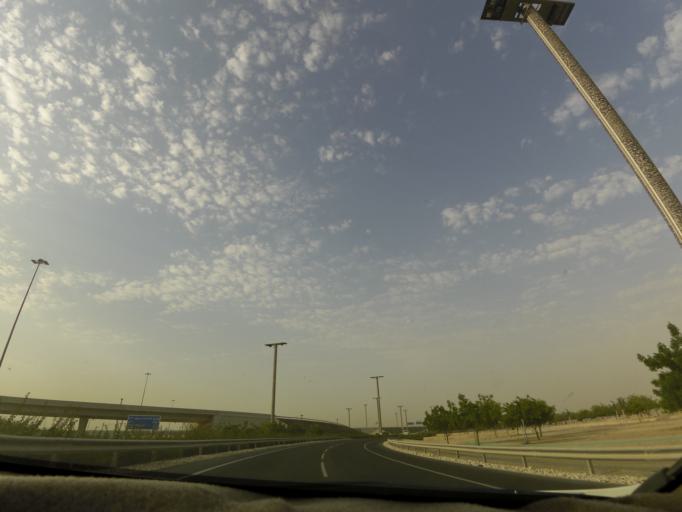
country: QA
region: Al Wakrah
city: Al Wakrah
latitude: 25.2429
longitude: 51.5897
